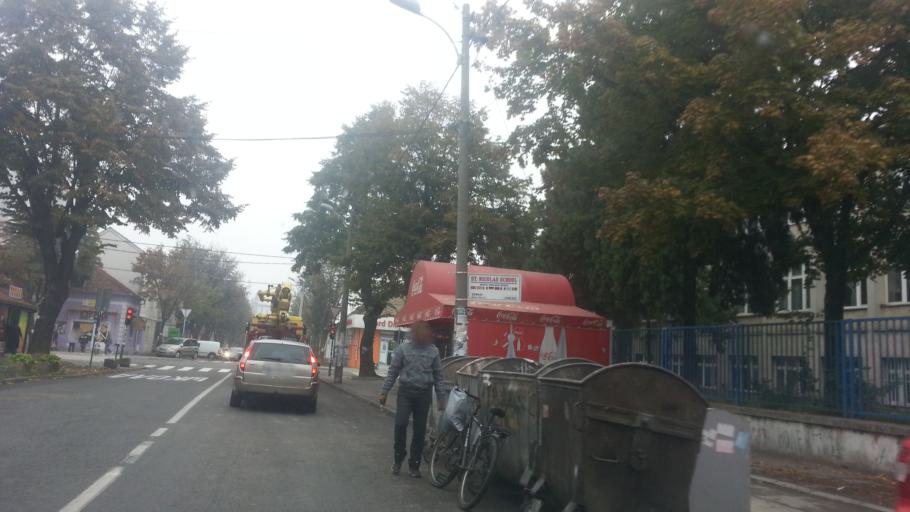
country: RS
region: Central Serbia
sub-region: Belgrade
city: Zemun
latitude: 44.8416
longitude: 20.3846
